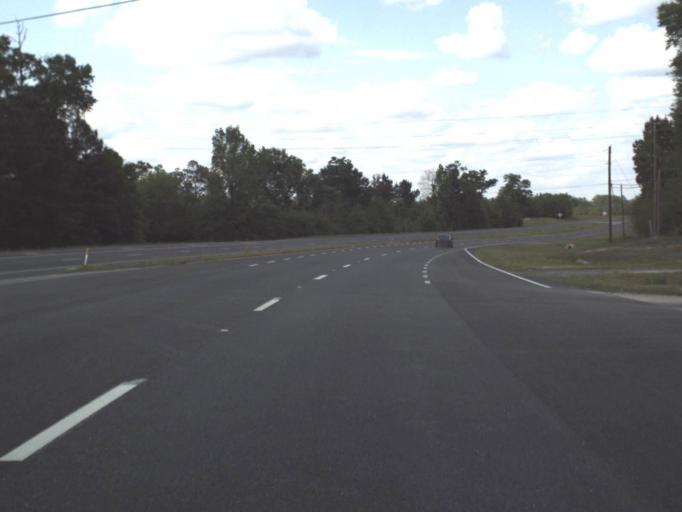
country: US
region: Florida
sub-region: Escambia County
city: Century
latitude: 30.9361
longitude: -87.2945
